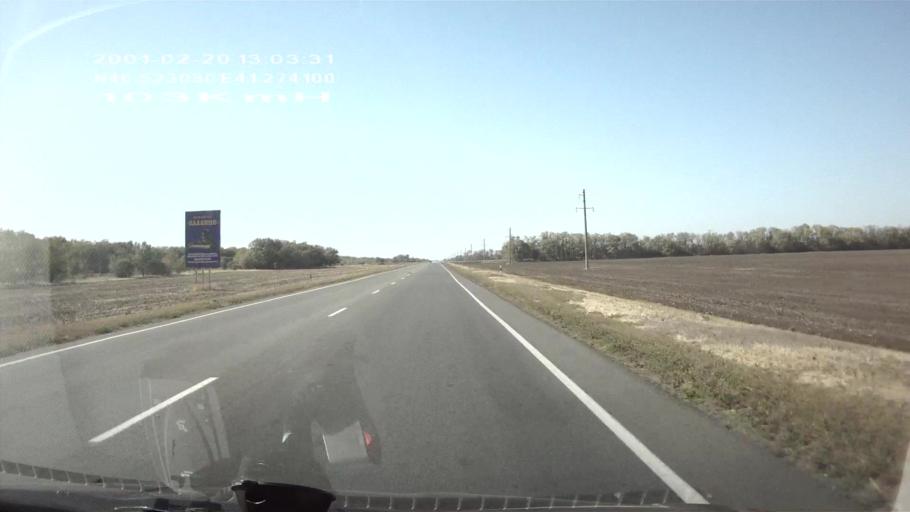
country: RU
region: Rostov
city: Gigant
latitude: 46.5240
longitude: 41.2709
